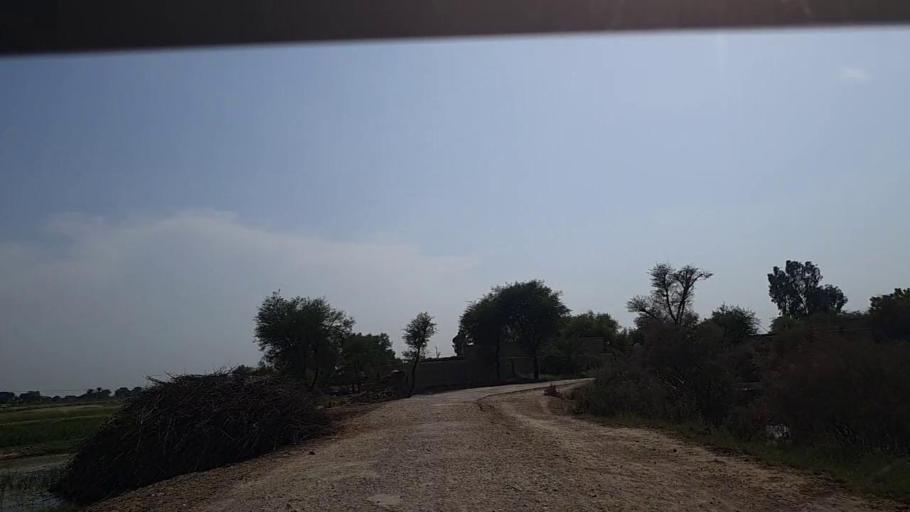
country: PK
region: Sindh
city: Khanpur
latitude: 27.8489
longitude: 69.3559
